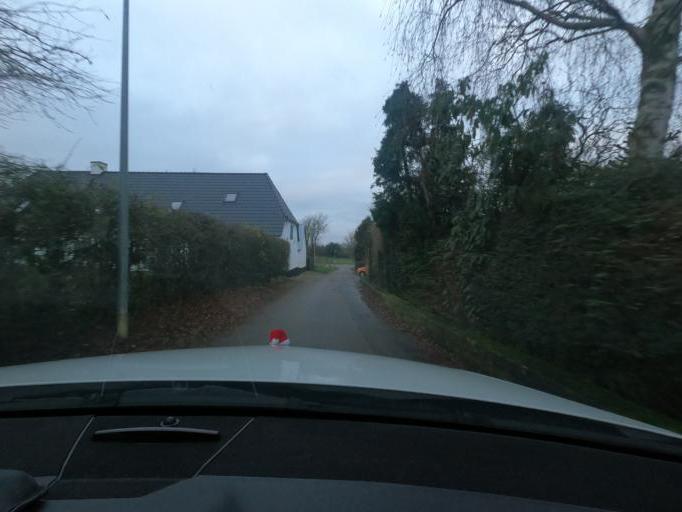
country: DK
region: South Denmark
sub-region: Sonderborg Kommune
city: Sonderborg
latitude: 54.9050
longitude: 9.8497
